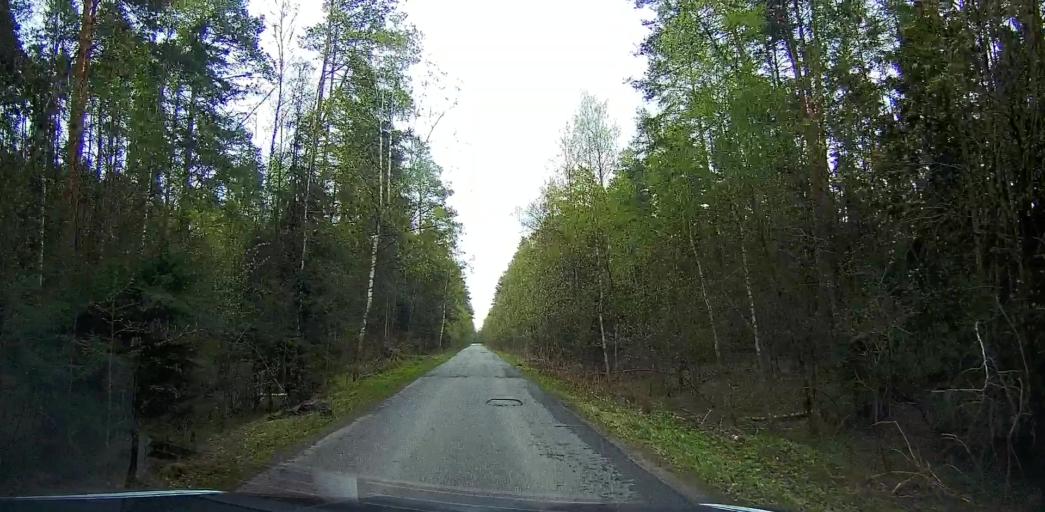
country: RU
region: Moskovskaya
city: Malyshevo
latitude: 55.5470
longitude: 38.3685
